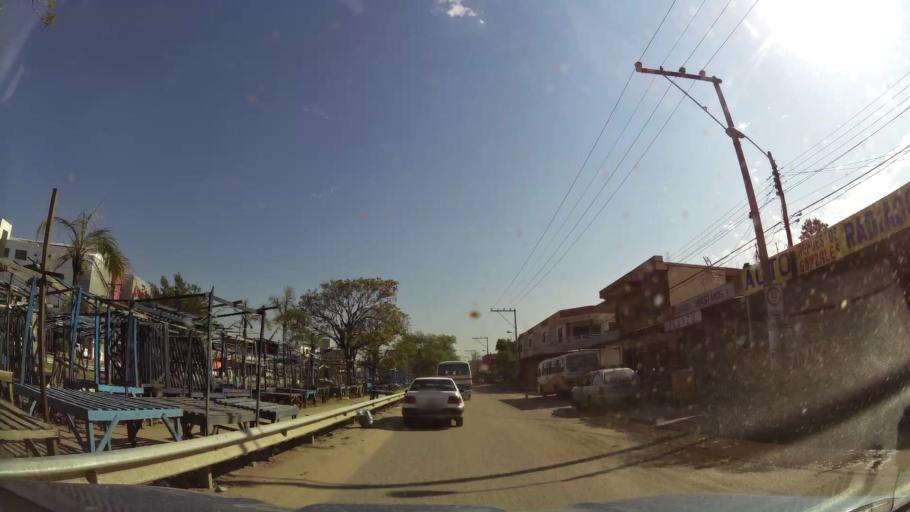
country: BO
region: Santa Cruz
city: Santa Cruz de la Sierra
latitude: -17.8272
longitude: -63.1361
